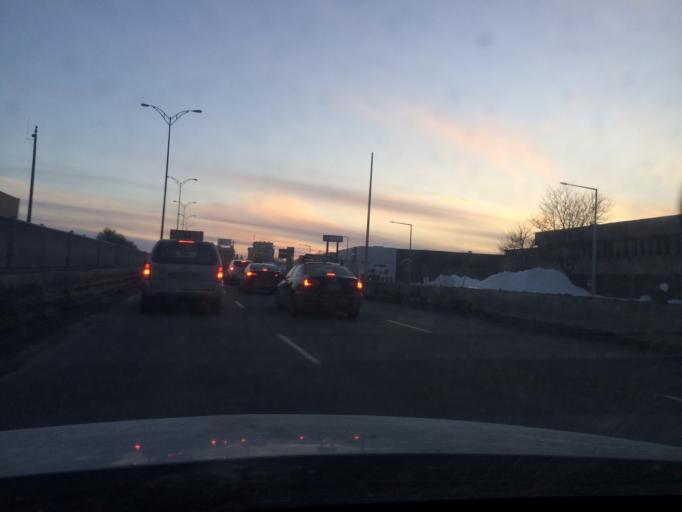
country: CA
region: Quebec
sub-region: Montreal
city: Saint-Leonard
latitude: 45.5736
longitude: -73.5968
